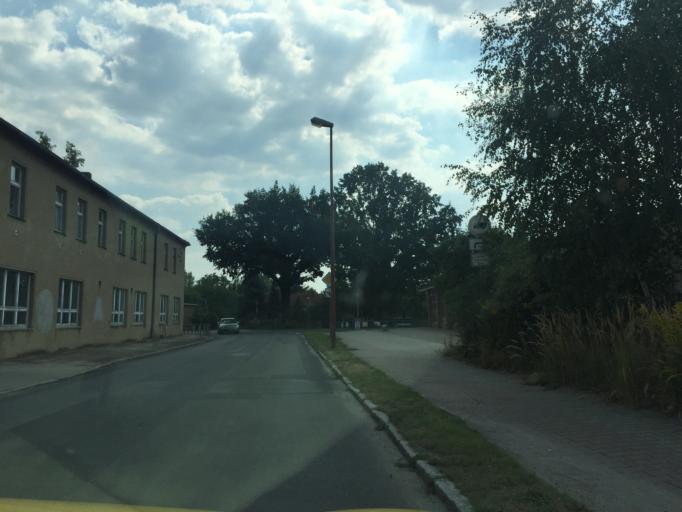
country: DE
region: Brandenburg
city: Welzow
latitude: 51.5722
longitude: 14.1730
